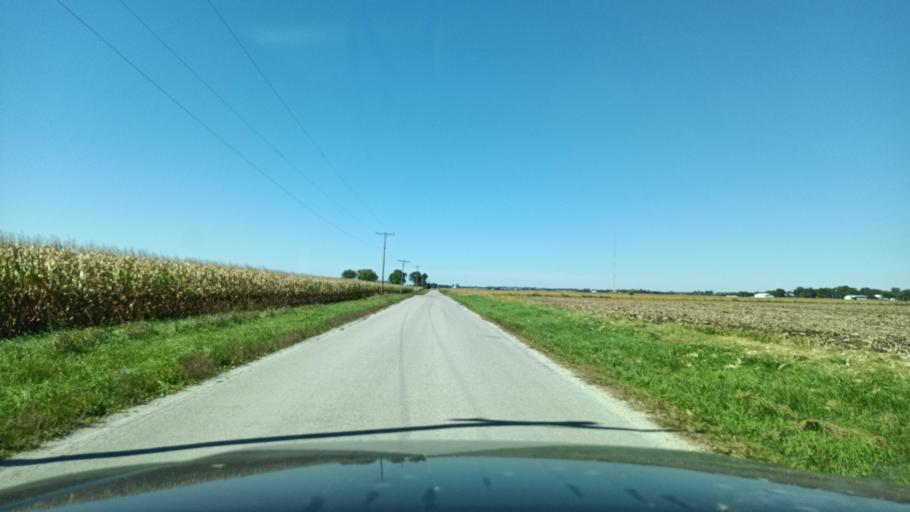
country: US
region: Illinois
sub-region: Champaign County
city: Mahomet
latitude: 40.0987
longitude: -88.4134
